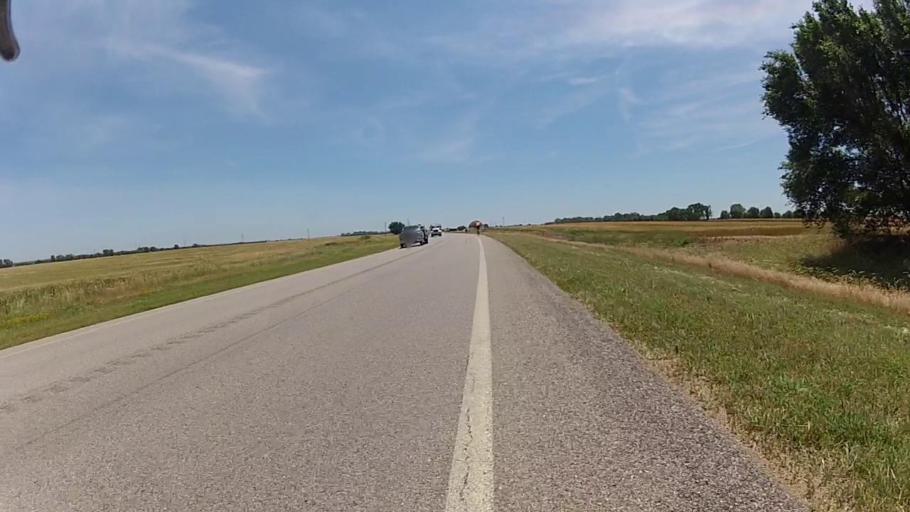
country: US
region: Kansas
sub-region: Barber County
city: Medicine Lodge
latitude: 37.2544
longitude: -98.5181
